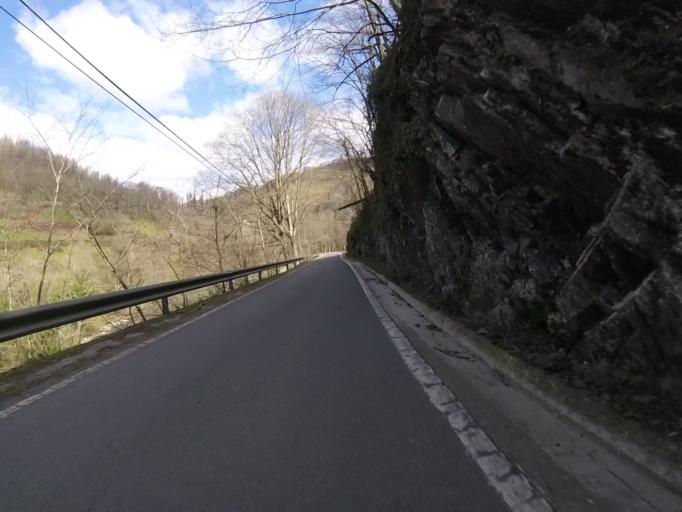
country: ES
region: Navarre
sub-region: Provincia de Navarra
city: Goizueta
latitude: 43.1564
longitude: -1.8504
